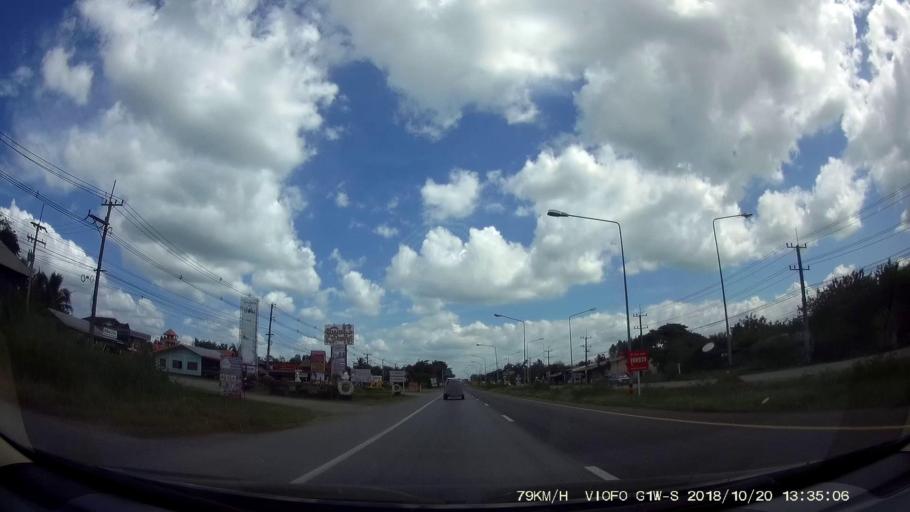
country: TH
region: Khon Kaen
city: Chum Phae
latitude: 16.5702
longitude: 102.0428
